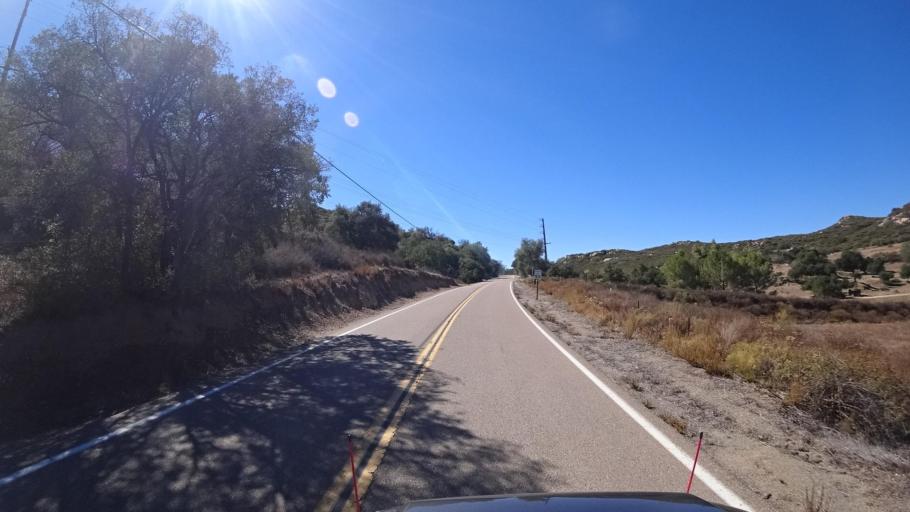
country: US
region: California
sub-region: San Diego County
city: Descanso
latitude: 32.7859
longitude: -116.6645
